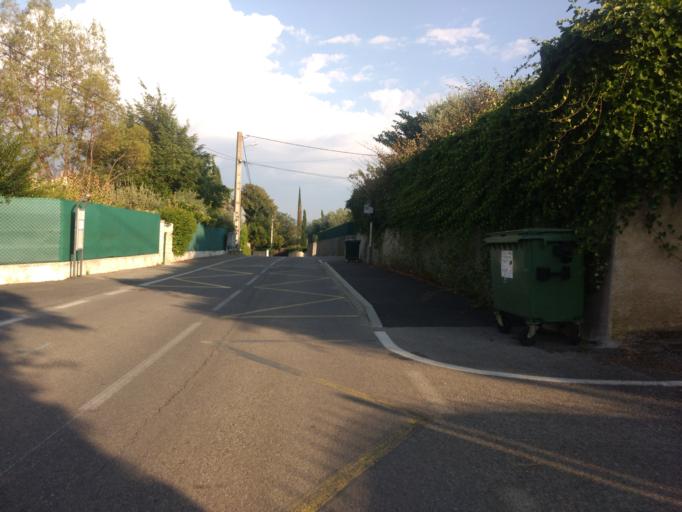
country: FR
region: Provence-Alpes-Cote d'Azur
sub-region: Departement des Alpes-de-Haute-Provence
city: Manosque
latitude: 43.8237
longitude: 5.7793
